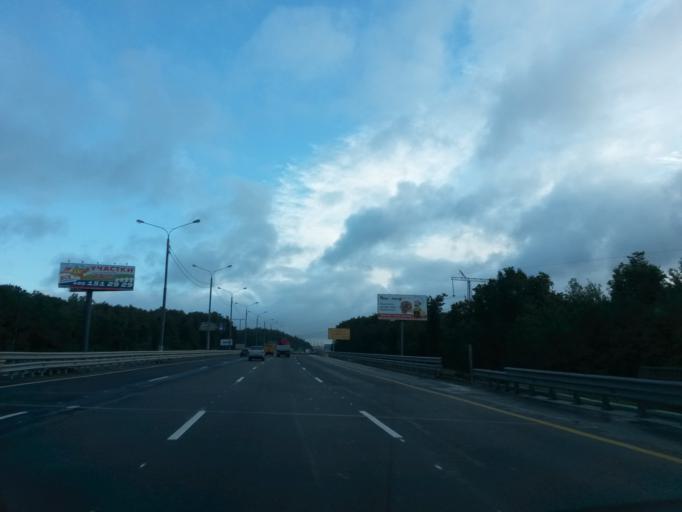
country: RU
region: Moscow
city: Annino
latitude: 55.5446
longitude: 37.6071
